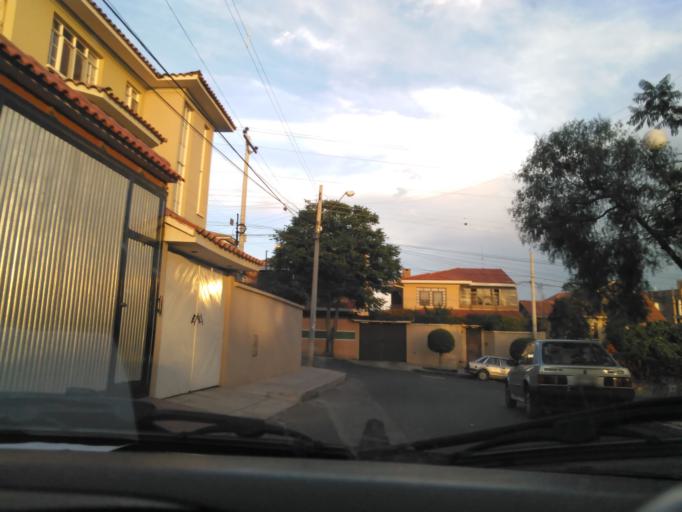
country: BO
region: Cochabamba
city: Cochabamba
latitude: -17.3727
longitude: -66.1380
